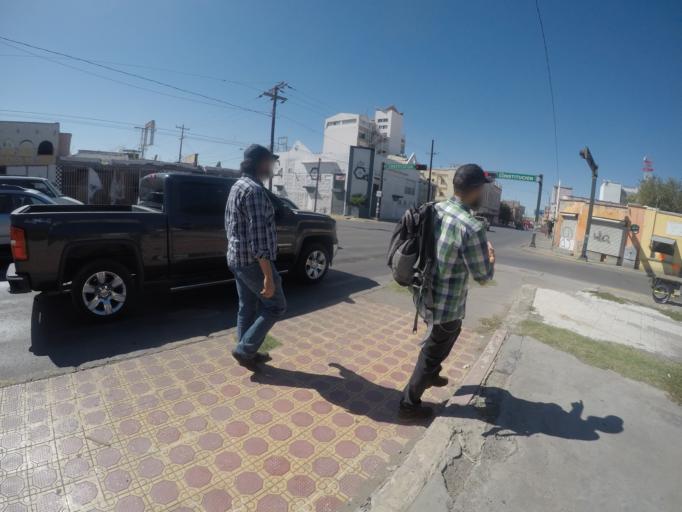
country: MX
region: Chihuahua
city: Ciudad Juarez
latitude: 31.7389
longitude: -106.4773
